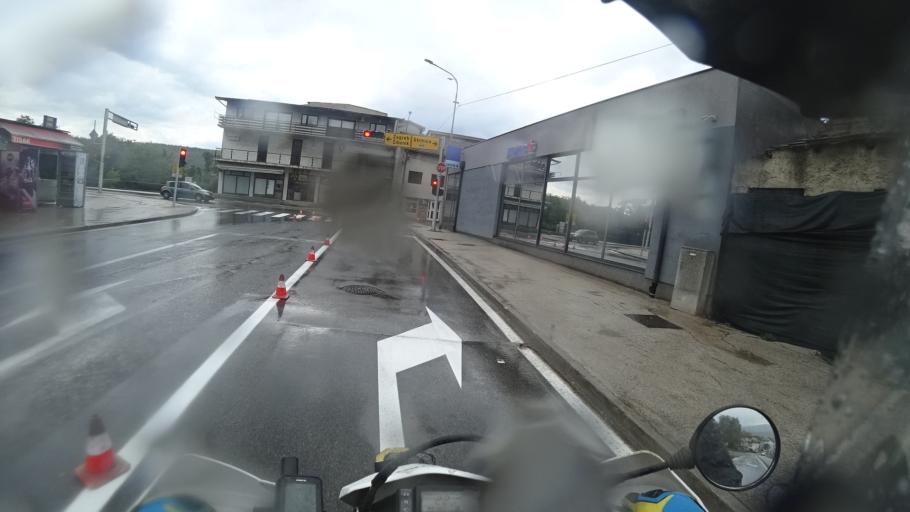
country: HR
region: Sibensko-Kniniska
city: Knin
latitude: 44.0424
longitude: 16.1979
